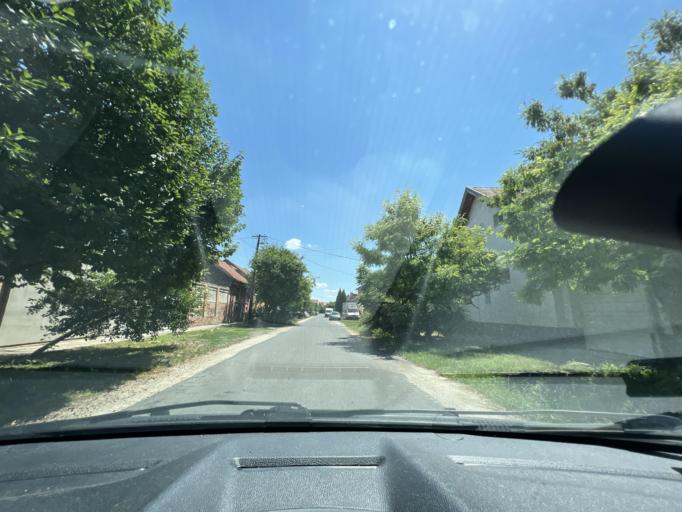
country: HU
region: Csongrad
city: Szeged
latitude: 46.2471
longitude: 20.1286
